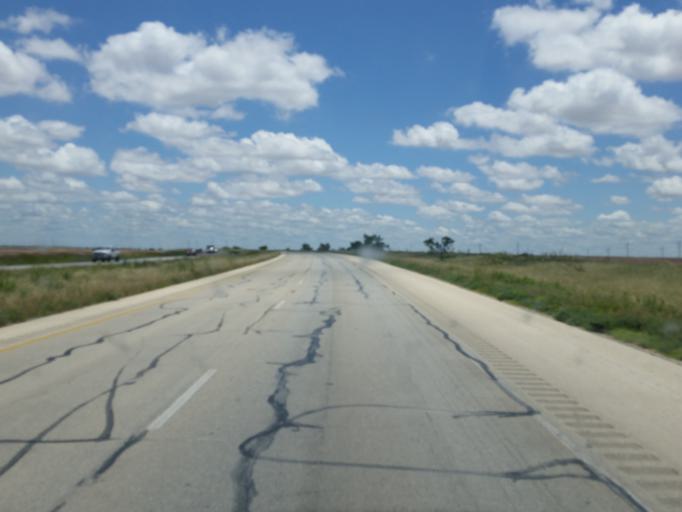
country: US
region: Texas
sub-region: Nolan County
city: Roscoe
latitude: 32.4913
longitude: -100.6334
